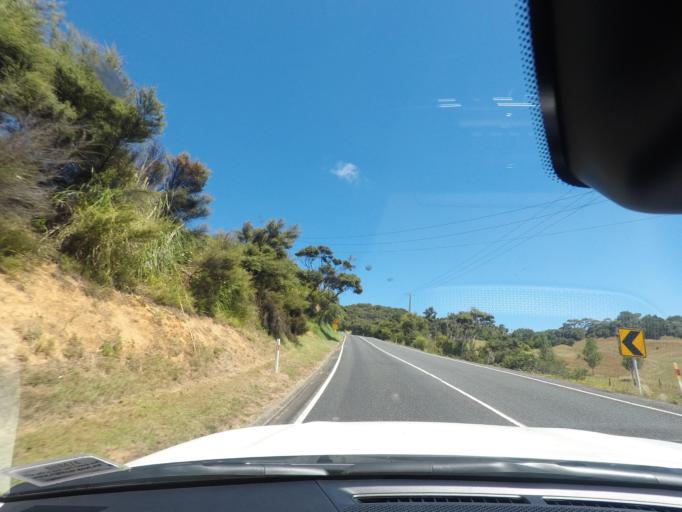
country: NZ
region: Auckland
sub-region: Auckland
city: Parakai
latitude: -36.5814
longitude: 174.3293
